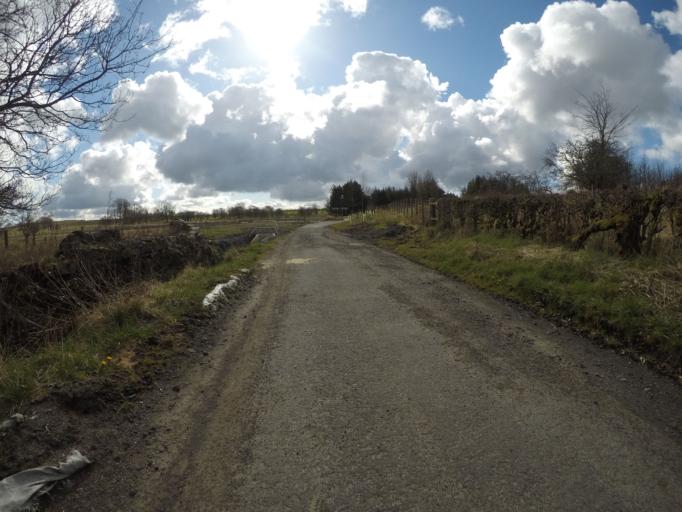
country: GB
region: Scotland
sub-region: North Ayrshire
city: Kilbirnie
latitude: 55.7274
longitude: -4.6660
